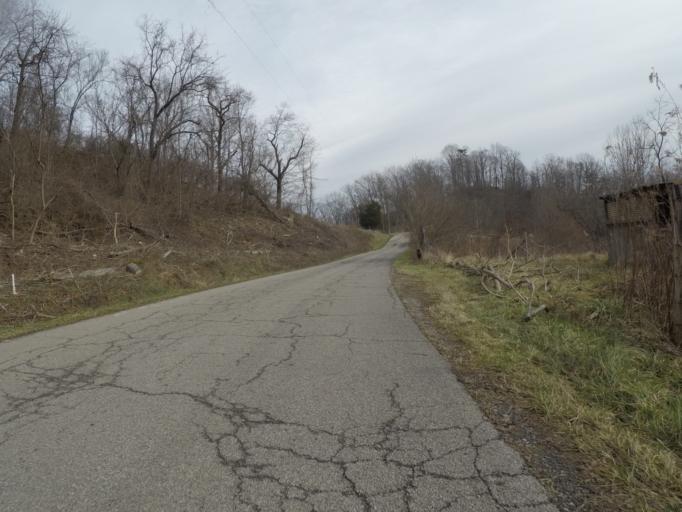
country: US
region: West Virginia
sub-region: Wayne County
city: Lavalette
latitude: 38.3446
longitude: -82.3797
